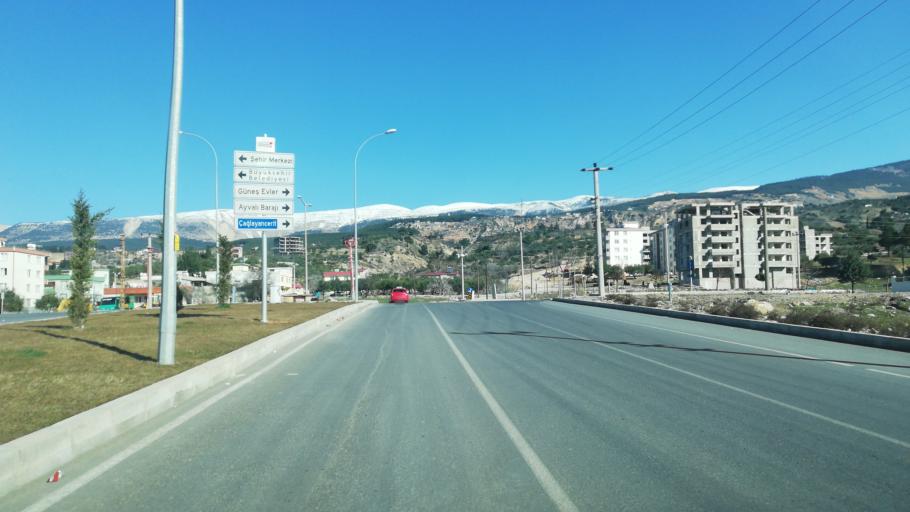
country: TR
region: Kahramanmaras
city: Kahramanmaras
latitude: 37.5816
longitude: 36.9745
